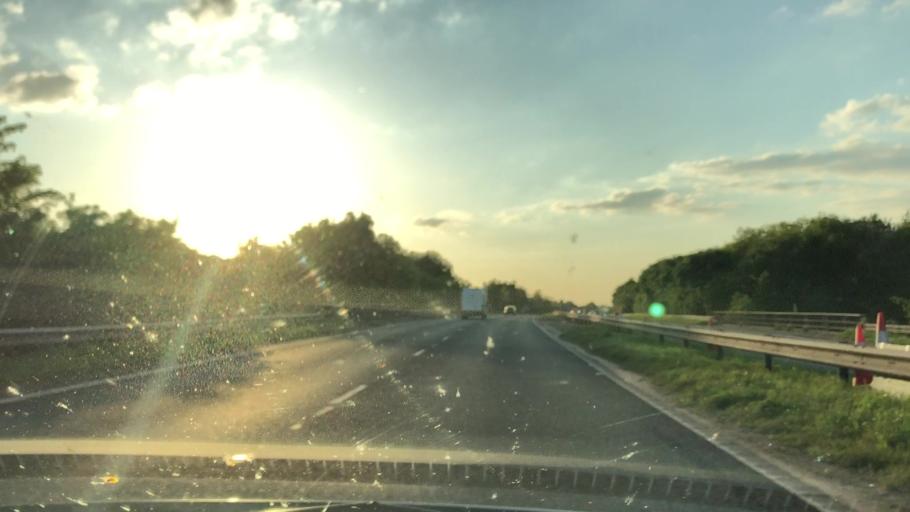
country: GB
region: England
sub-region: Cheshire West and Chester
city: Guilden Sutton
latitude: 53.2110
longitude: -2.8513
